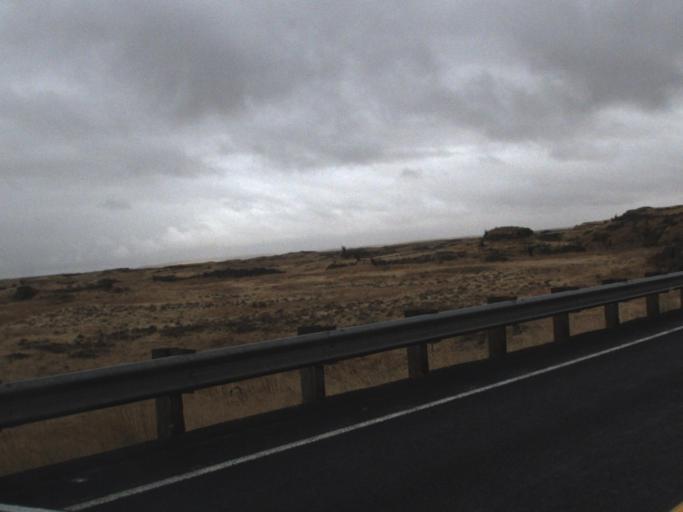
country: US
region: Washington
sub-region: Spokane County
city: Medical Lake
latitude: 47.2663
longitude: -117.9330
